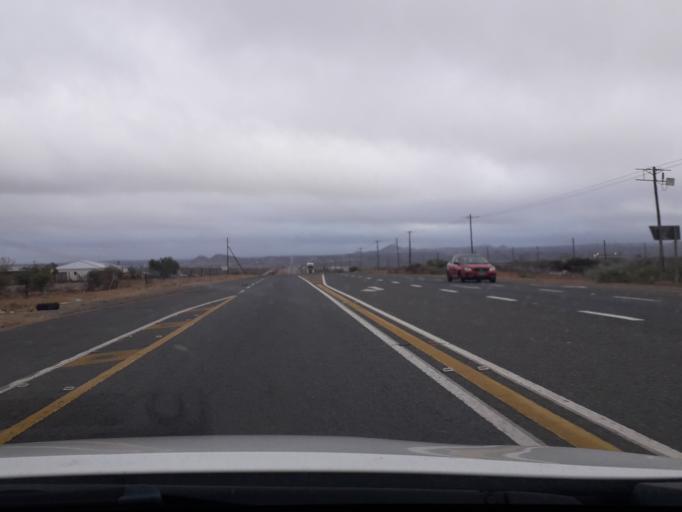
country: ZA
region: Limpopo
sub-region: Capricorn District Municipality
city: Dendron
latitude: -23.4751
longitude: 29.7302
